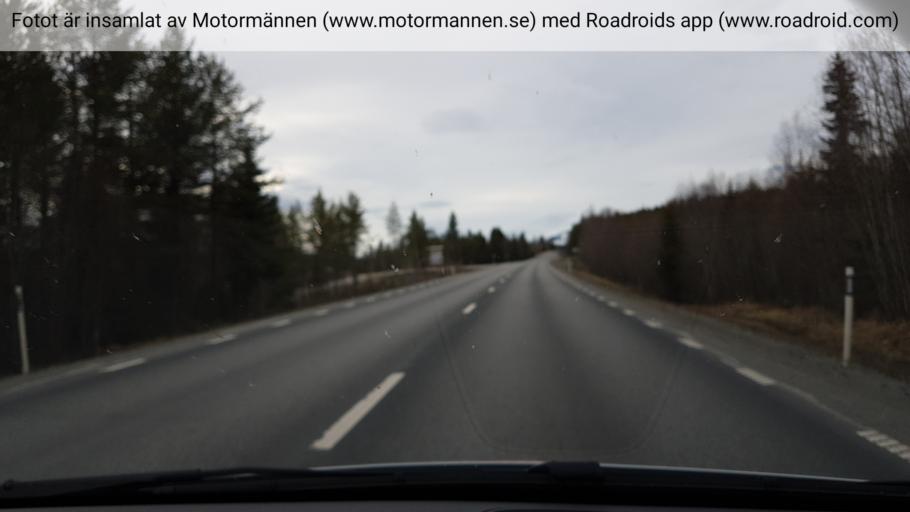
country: SE
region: Jaemtland
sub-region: Are Kommun
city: Are
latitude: 63.3302
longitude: 13.2220
